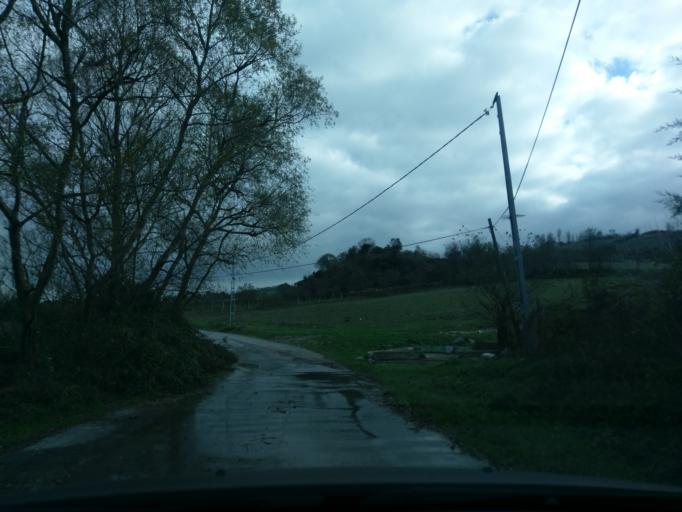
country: TR
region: Istanbul
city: Durusu
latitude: 41.2680
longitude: 28.6747
